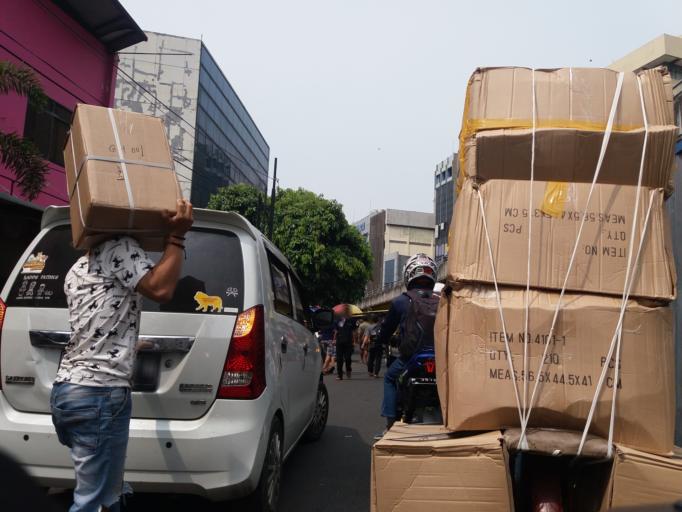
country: ID
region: Jakarta Raya
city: Jakarta
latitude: -6.1390
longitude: 106.8118
